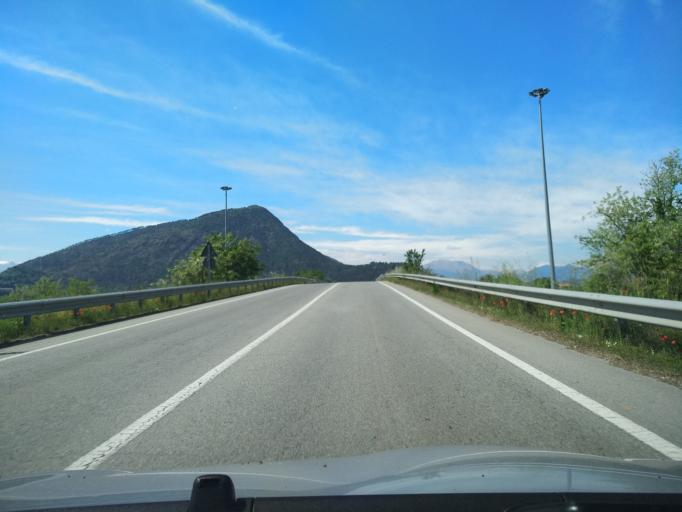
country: IT
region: Piedmont
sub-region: Provincia di Torino
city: Piossasco
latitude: 44.9785
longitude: 7.4745
